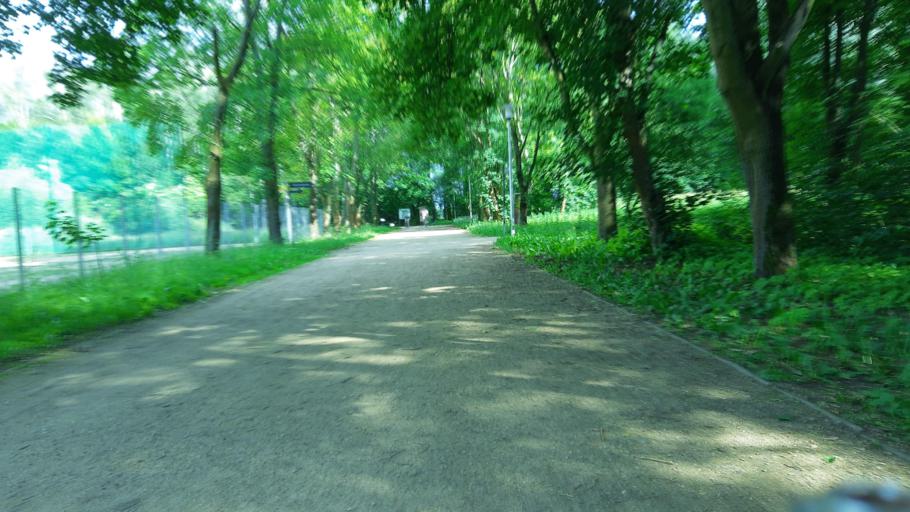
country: PL
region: Lodz Voivodeship
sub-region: Powiat sieradzki
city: Sieradz
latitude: 51.5958
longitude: 18.7549
